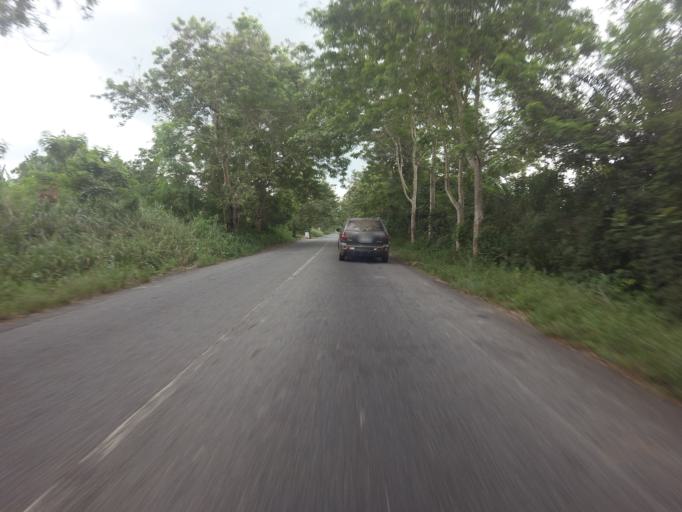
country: GH
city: Akropong
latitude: 5.9575
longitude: -0.1153
